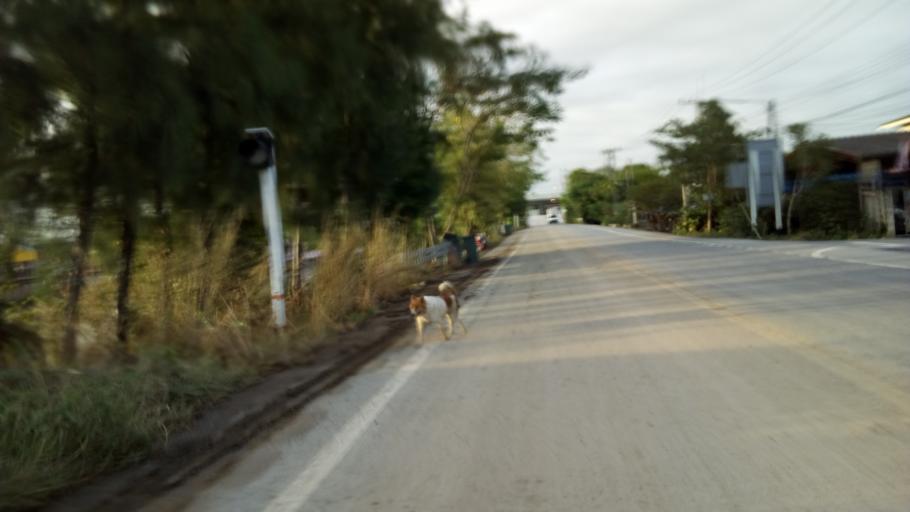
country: TH
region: Pathum Thani
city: Nong Suea
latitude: 14.0753
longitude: 100.8947
